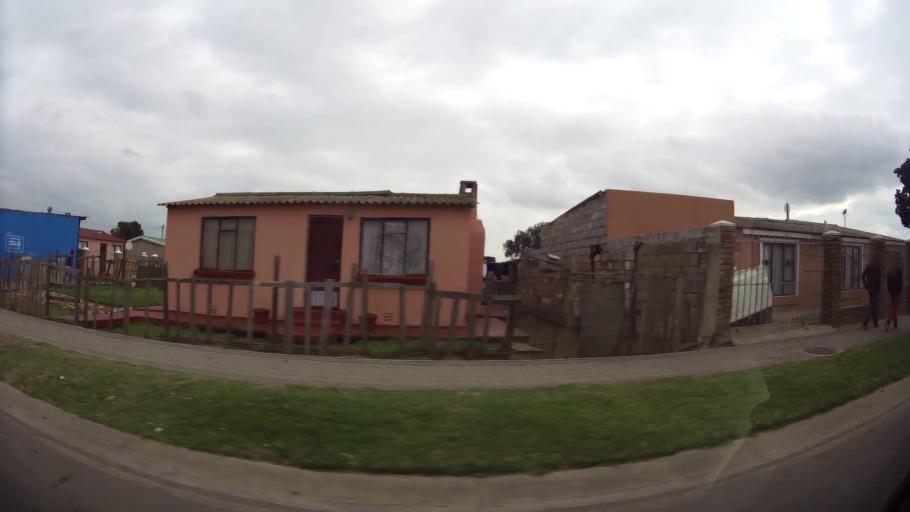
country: ZA
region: Eastern Cape
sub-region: Nelson Mandela Bay Metropolitan Municipality
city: Port Elizabeth
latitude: -33.8869
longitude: 25.5954
